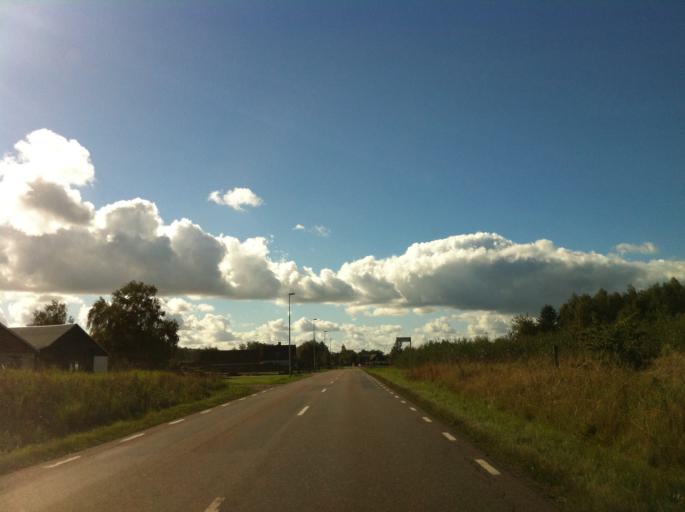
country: SE
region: Skane
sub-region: Sjobo Kommun
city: Sjoebo
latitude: 55.6334
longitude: 13.7374
